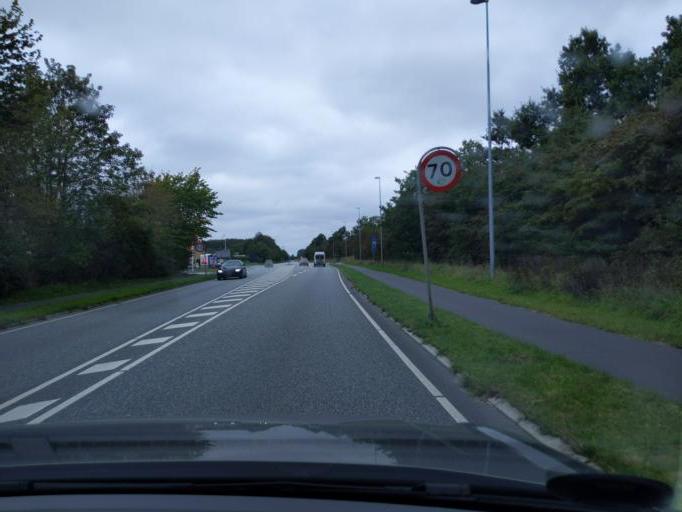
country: DK
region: Central Jutland
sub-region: Randers Kommune
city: Randers
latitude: 56.4824
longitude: 9.9959
